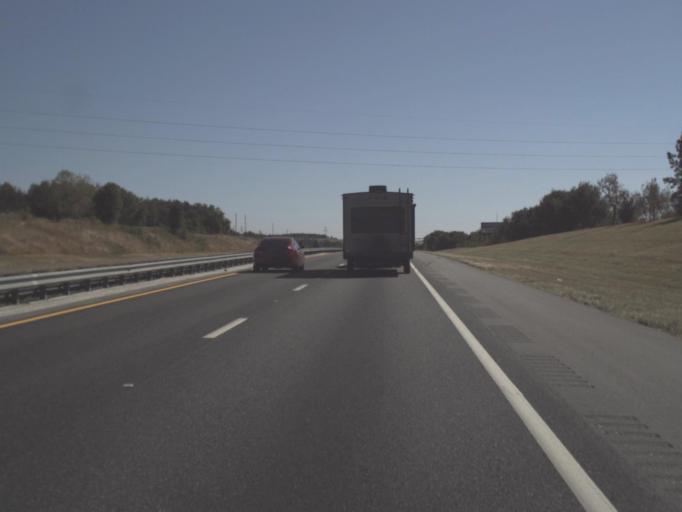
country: US
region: Florida
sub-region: Lake County
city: Minneola
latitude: 28.6291
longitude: -81.7655
